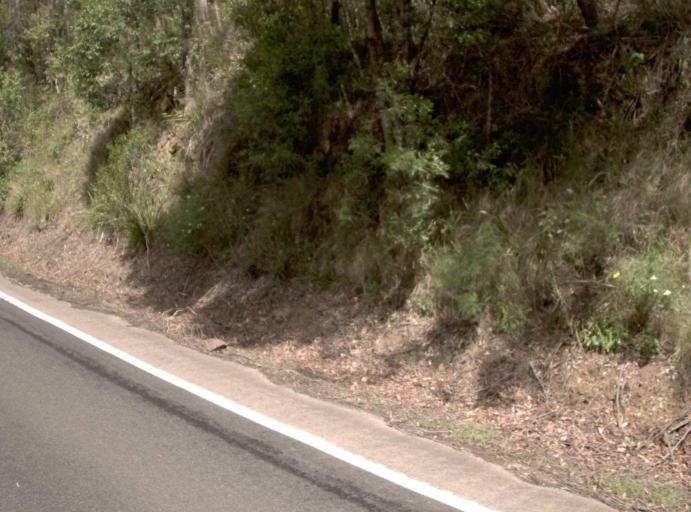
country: AU
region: New South Wales
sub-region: Bombala
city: Bombala
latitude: -37.5349
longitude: 149.3783
